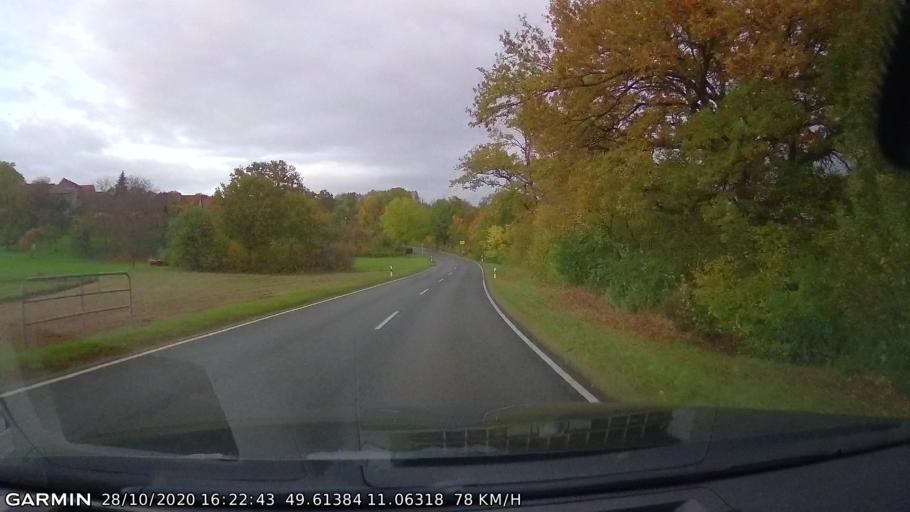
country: DE
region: Bavaria
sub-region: Regierungsbezirk Mittelfranken
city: Marloffstein
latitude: 49.6137
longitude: 11.0633
